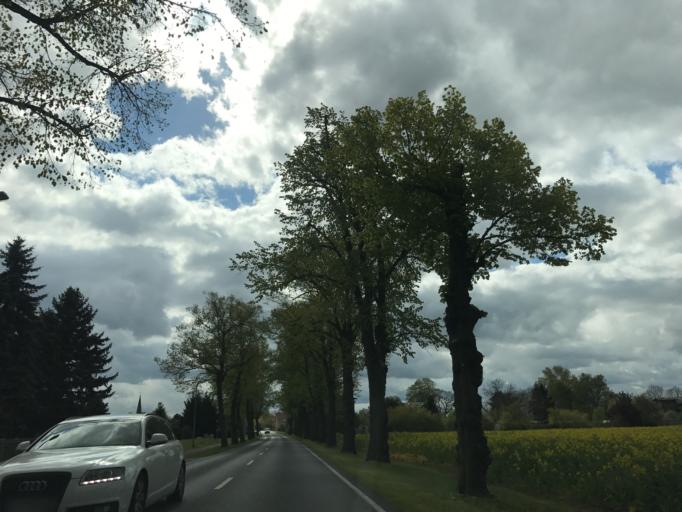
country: DE
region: Brandenburg
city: Roskow
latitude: 52.4753
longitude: 12.7088
